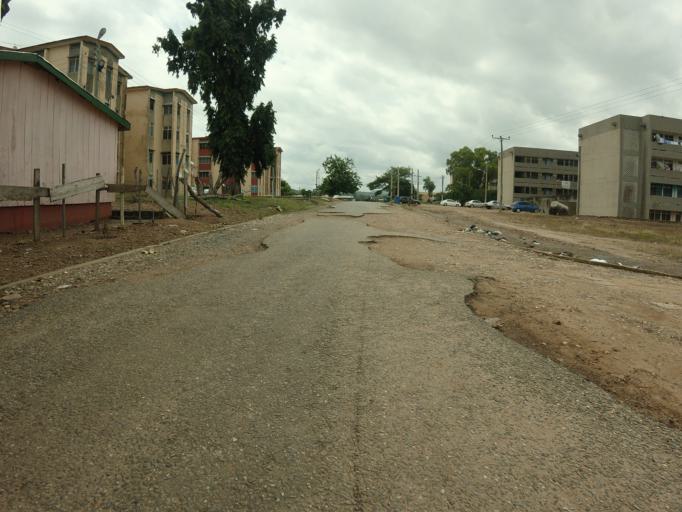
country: GH
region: Volta
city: Ho
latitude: 6.5915
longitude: 0.4606
